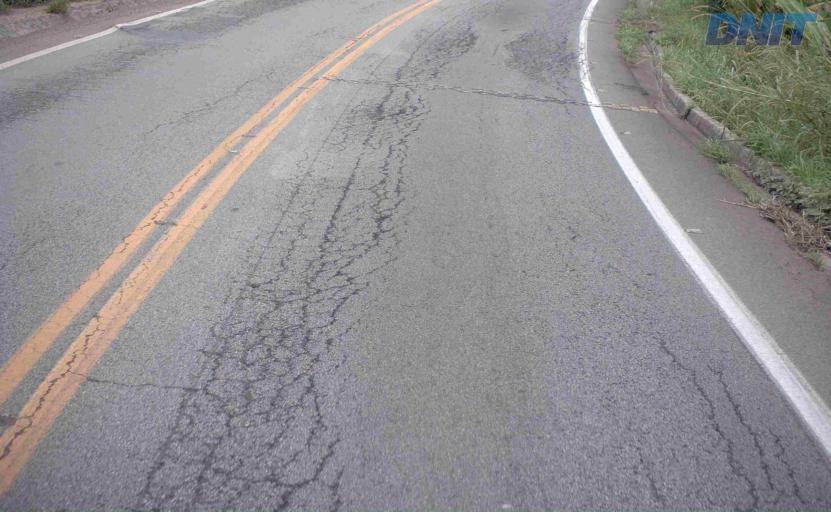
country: BR
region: Minas Gerais
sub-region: Nova Era
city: Nova Era
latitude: -19.7733
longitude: -43.0458
